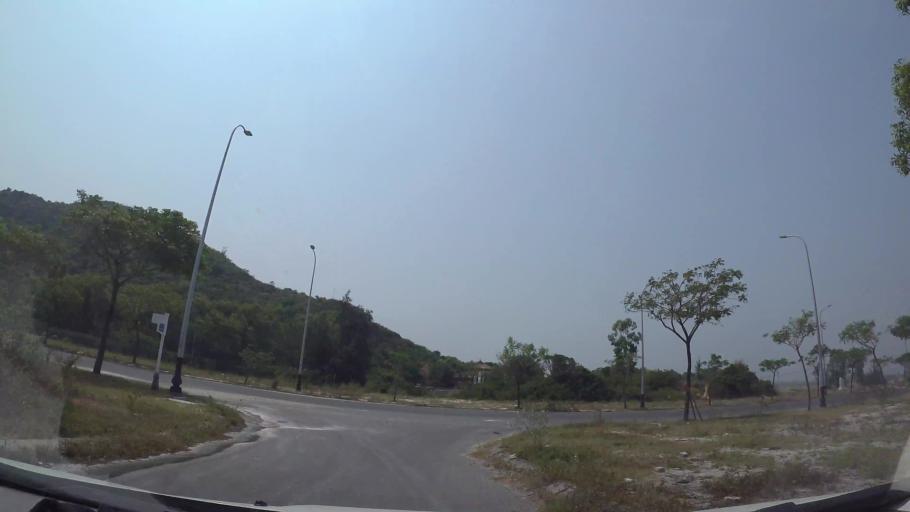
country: VN
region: Da Nang
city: Ngu Hanh Son
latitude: 16.0065
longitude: 108.2551
